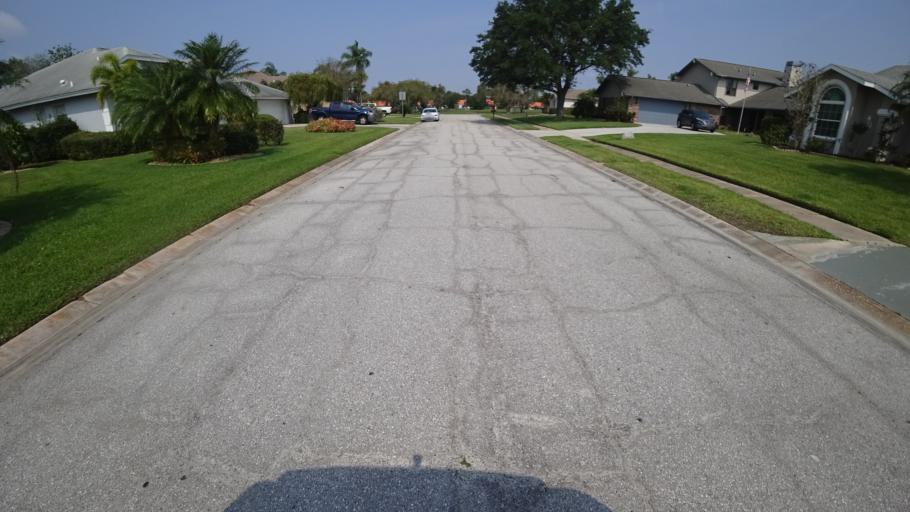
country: US
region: Florida
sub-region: Manatee County
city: Samoset
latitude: 27.4509
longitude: -82.5107
